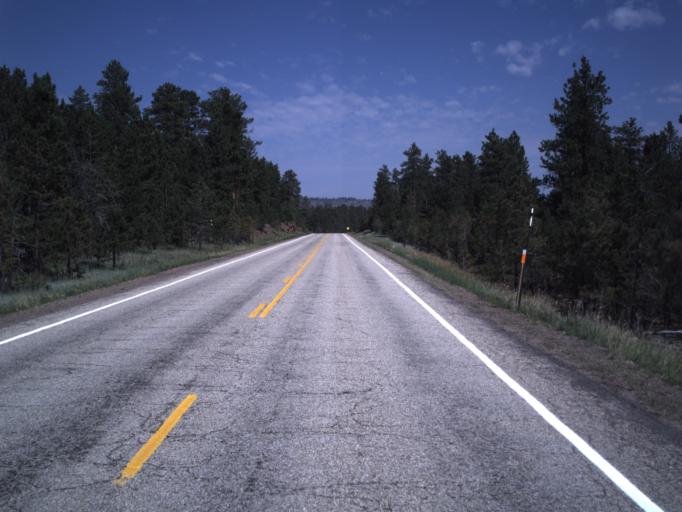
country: US
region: Utah
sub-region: Daggett County
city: Manila
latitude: 40.8507
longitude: -109.6725
